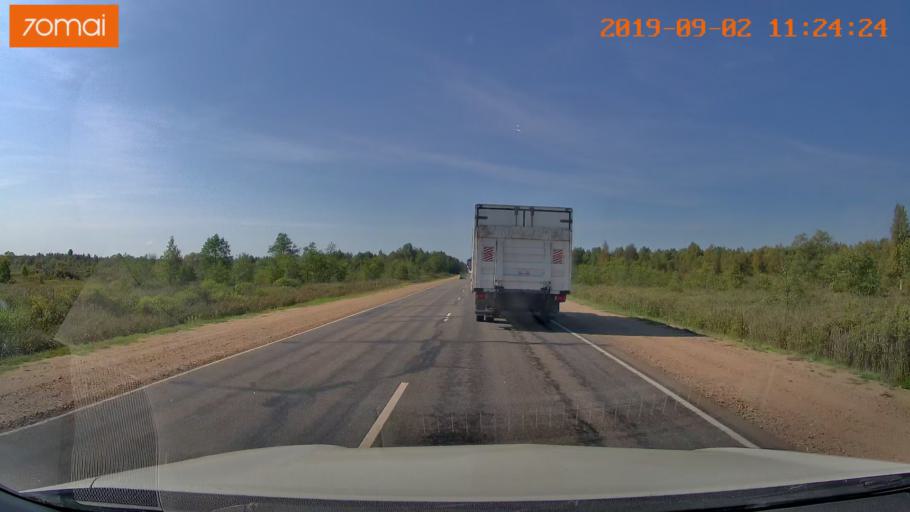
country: RU
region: Smolensk
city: Roslavl'
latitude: 54.0106
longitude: 32.9759
